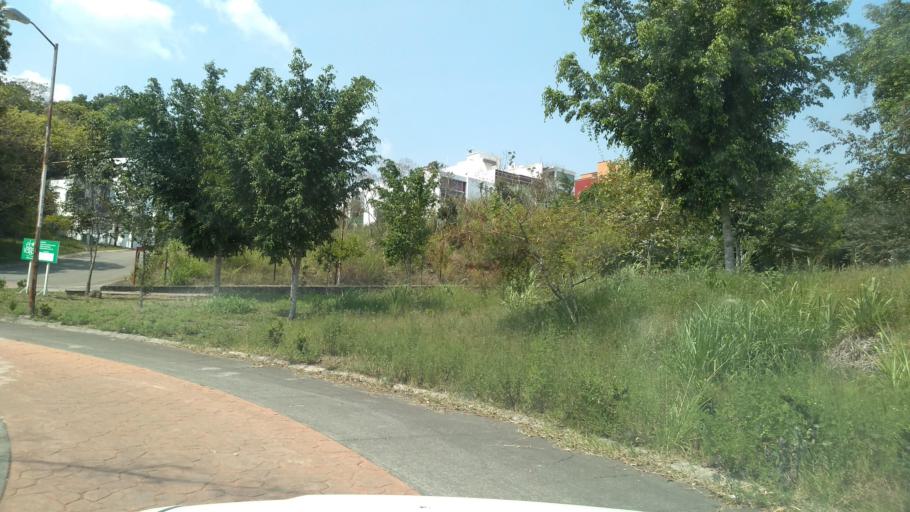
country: MX
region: Veracruz
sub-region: Emiliano Zapata
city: Las Trancas
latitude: 19.5138
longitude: -96.8607
